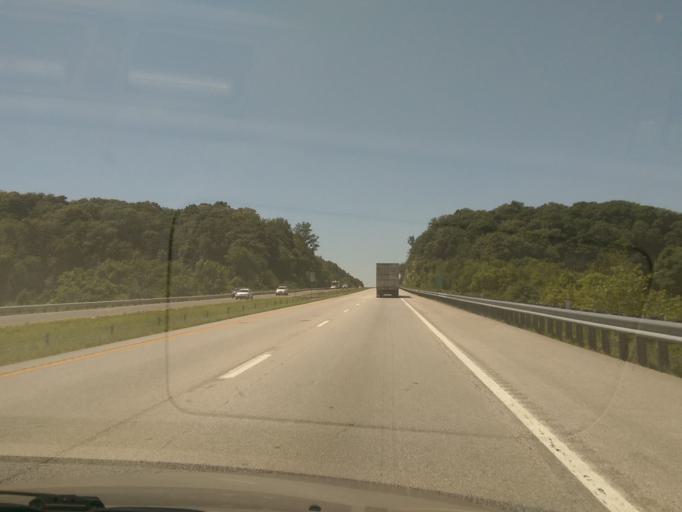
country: US
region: Missouri
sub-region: Cooper County
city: Boonville
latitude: 38.9340
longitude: -92.9454
